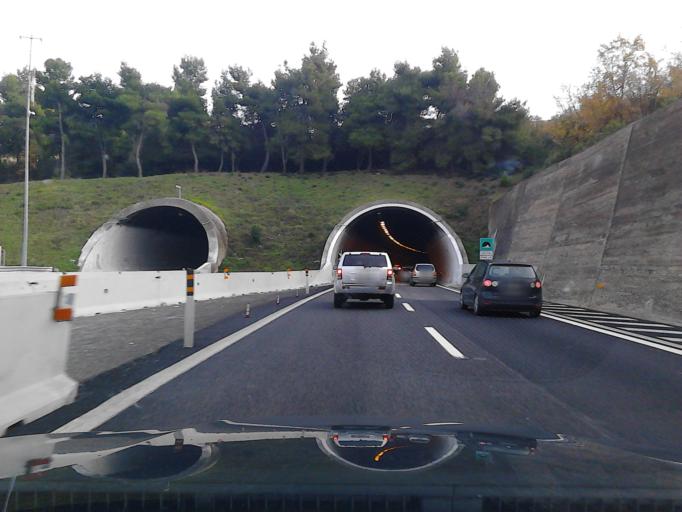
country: IT
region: Abruzzo
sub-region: Provincia di Teramo
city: Pineto
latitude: 42.6021
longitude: 14.0609
